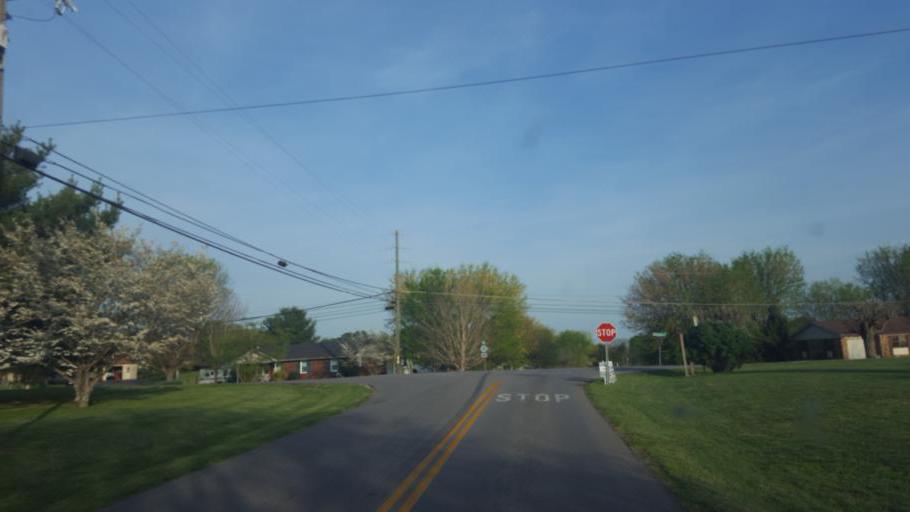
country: US
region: Kentucky
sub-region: Barren County
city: Glasgow
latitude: 36.9437
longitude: -85.9822
